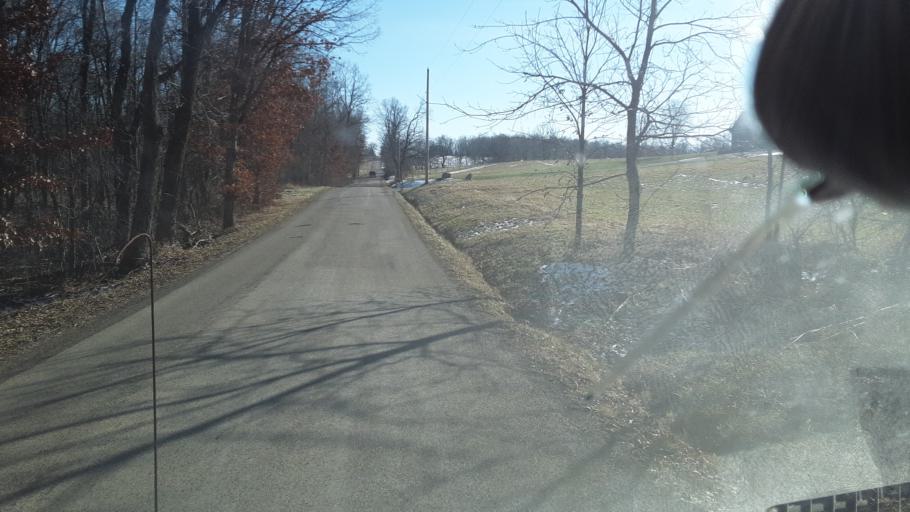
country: US
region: Ohio
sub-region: Ashland County
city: Loudonville
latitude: 40.7259
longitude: -82.2218
